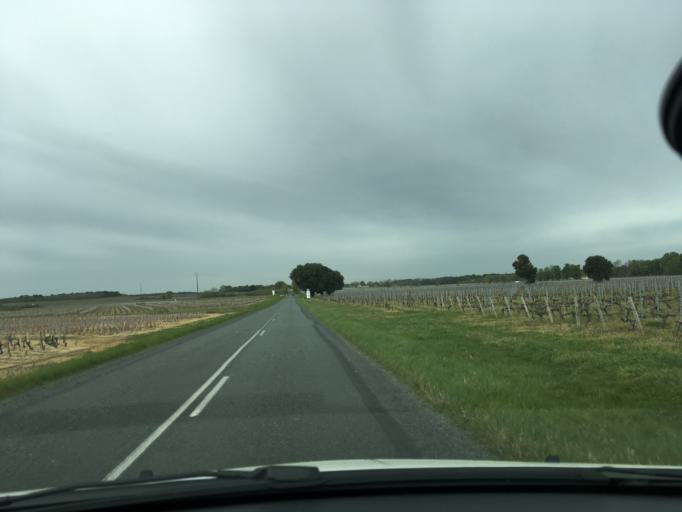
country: FR
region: Aquitaine
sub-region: Departement de la Gironde
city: Lesparre-Medoc
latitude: 45.3254
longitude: -0.8858
